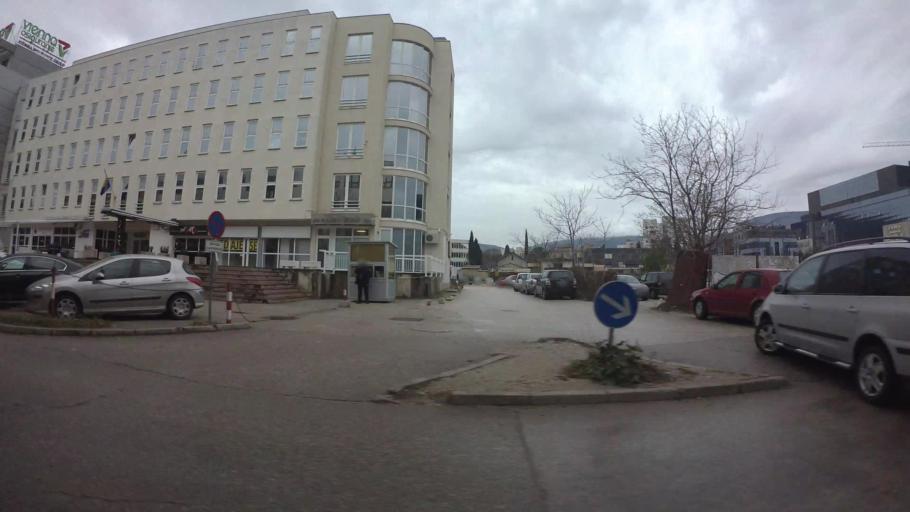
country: BA
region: Federation of Bosnia and Herzegovina
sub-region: Hercegovacko-Bosanski Kanton
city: Mostar
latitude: 43.3469
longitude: 17.8073
